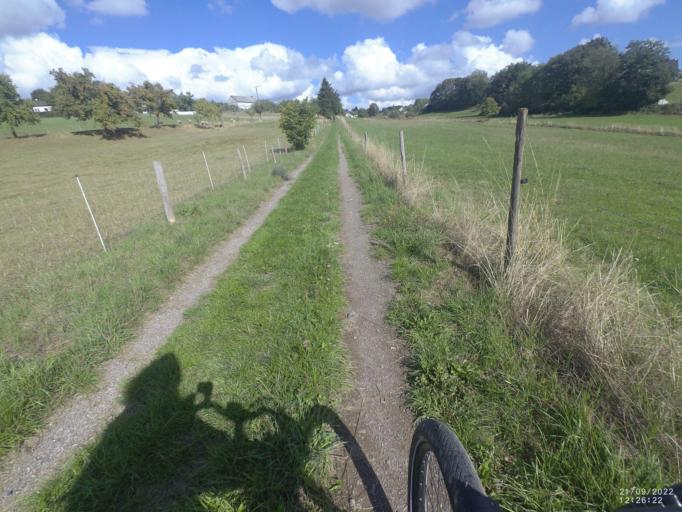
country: DE
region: Rheinland-Pfalz
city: Ellscheid
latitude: 50.1470
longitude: 6.9147
